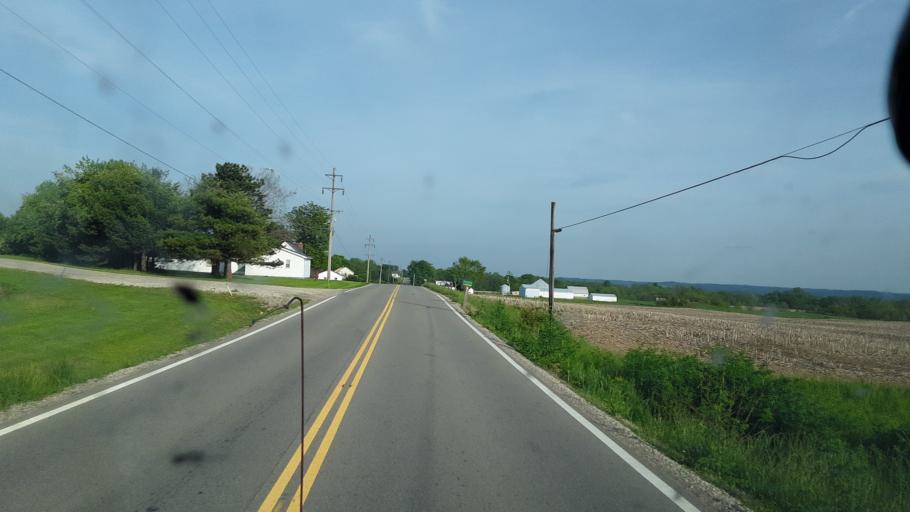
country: US
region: Ohio
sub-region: Ross County
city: Kingston
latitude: 39.5238
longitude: -82.8254
